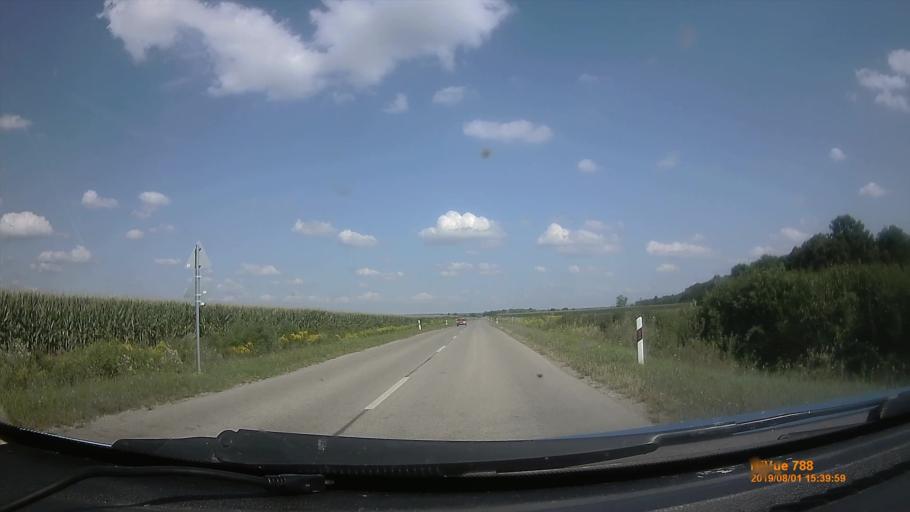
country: HU
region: Baranya
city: Szentlorinc
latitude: 45.9886
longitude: 17.9448
